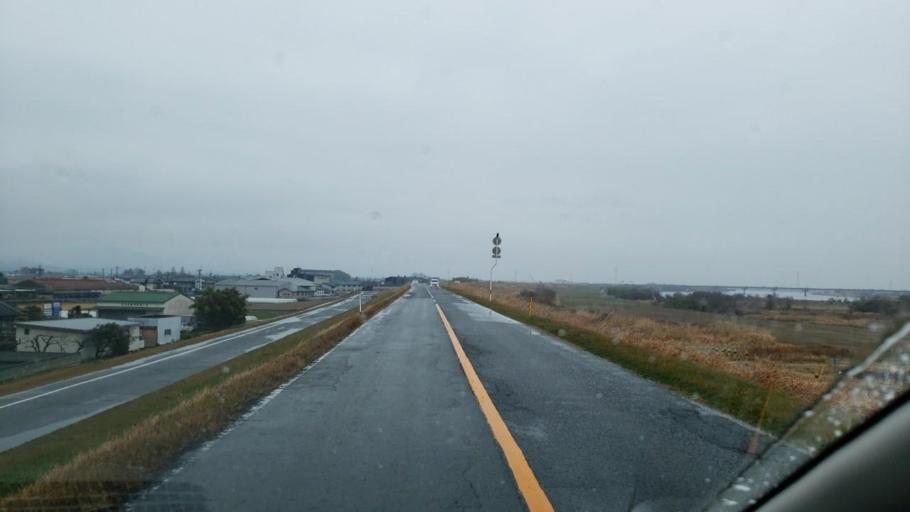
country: JP
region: Tokushima
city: Ishii
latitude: 34.1032
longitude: 134.4203
